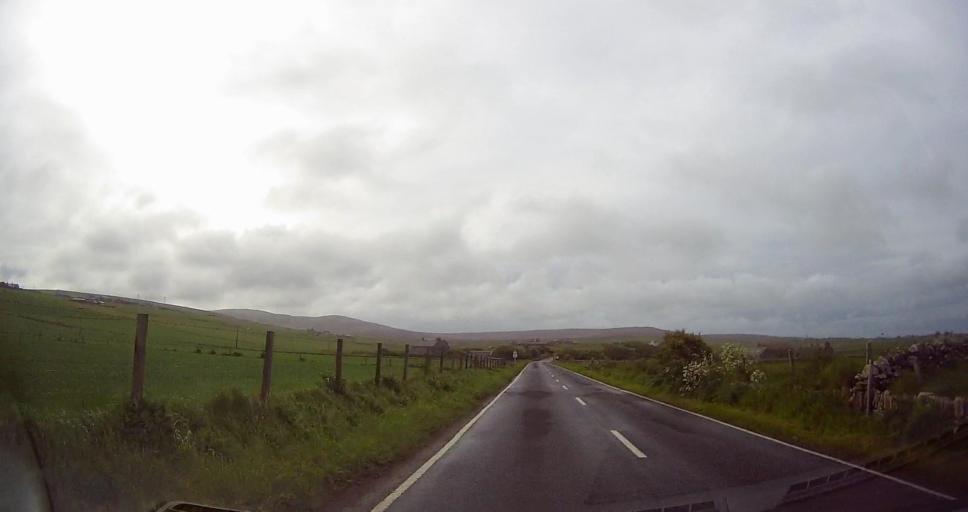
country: GB
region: Scotland
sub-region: Orkney Islands
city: Stromness
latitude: 58.9702
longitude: -3.2321
